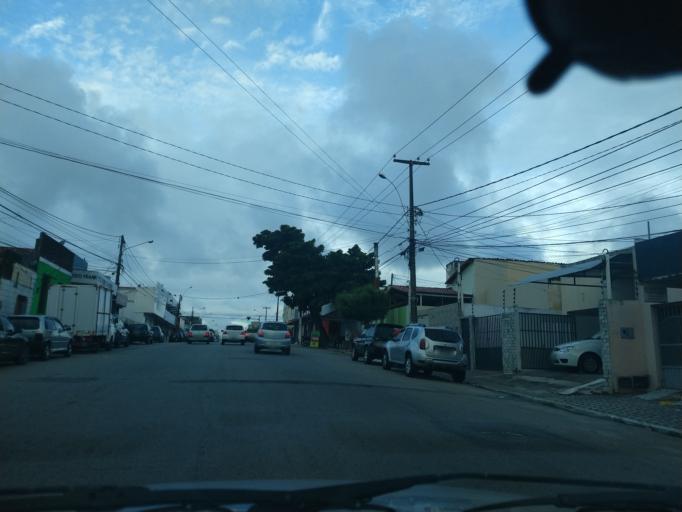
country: BR
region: Rio Grande do Norte
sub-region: Natal
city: Natal
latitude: -5.8001
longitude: -35.2218
